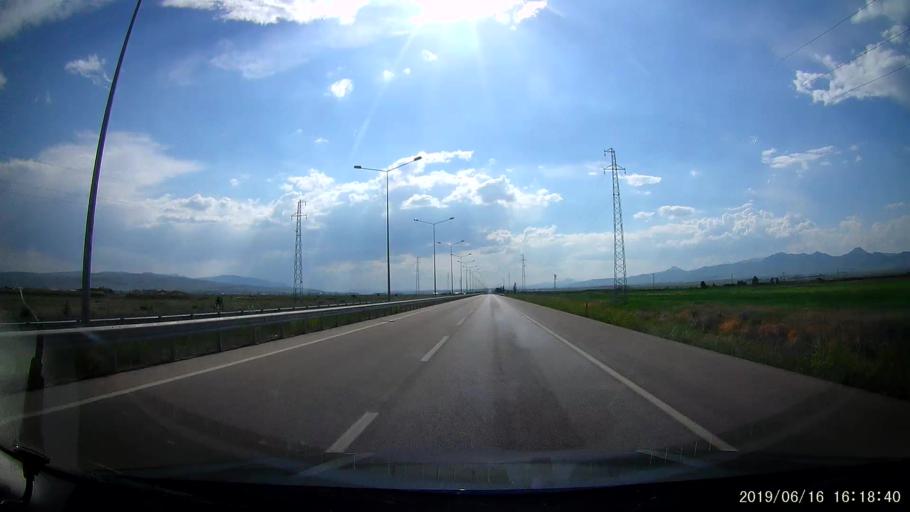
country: TR
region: Erzurum
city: Ilica
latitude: 39.9652
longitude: 41.1623
